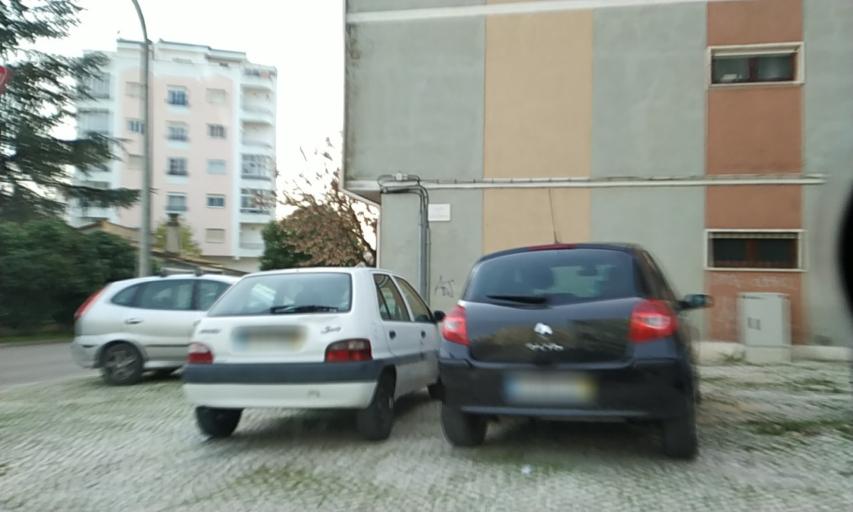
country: PT
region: Setubal
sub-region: Setubal
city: Setubal
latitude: 38.5334
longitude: -8.8769
